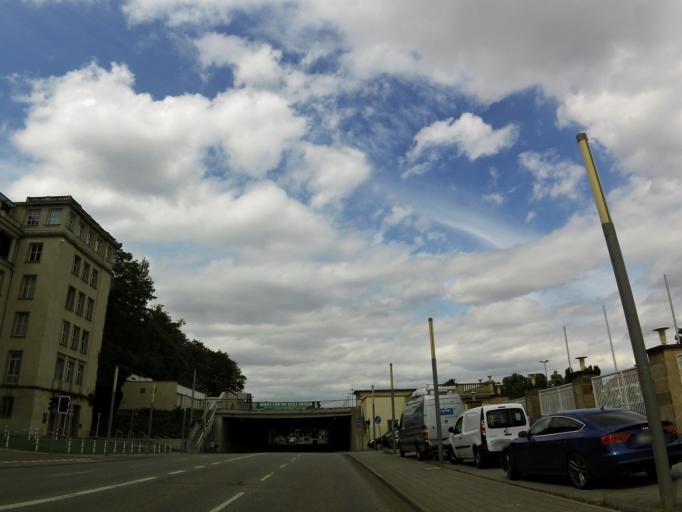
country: DE
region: Saxony
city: Leipzig
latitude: 51.3461
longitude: 12.3508
